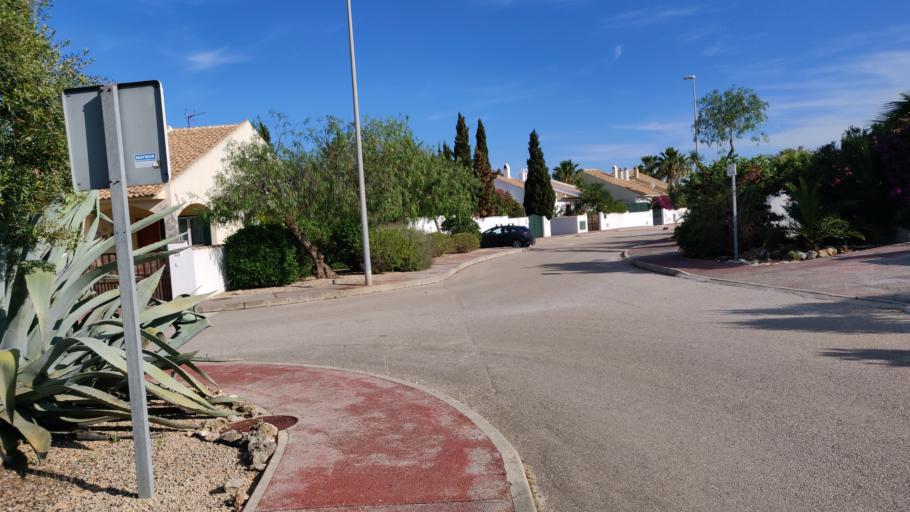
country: ES
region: Balearic Islands
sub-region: Illes Balears
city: Felanitx
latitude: 39.4522
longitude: 3.2603
